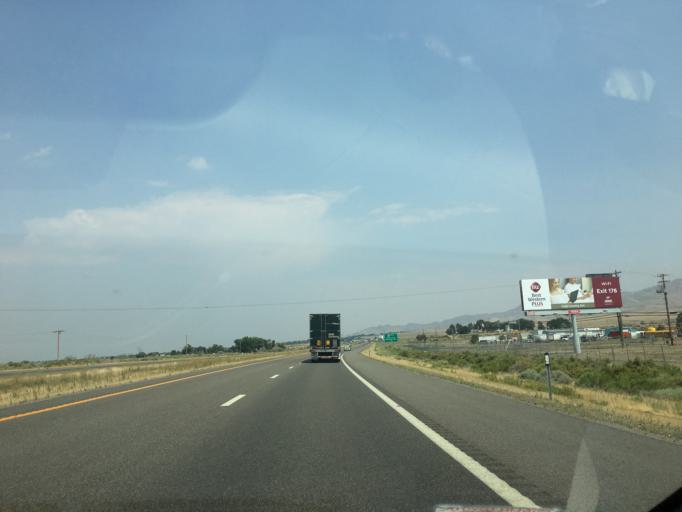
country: US
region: Nevada
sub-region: Humboldt County
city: Winnemucca
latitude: 40.9420
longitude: -117.7774
